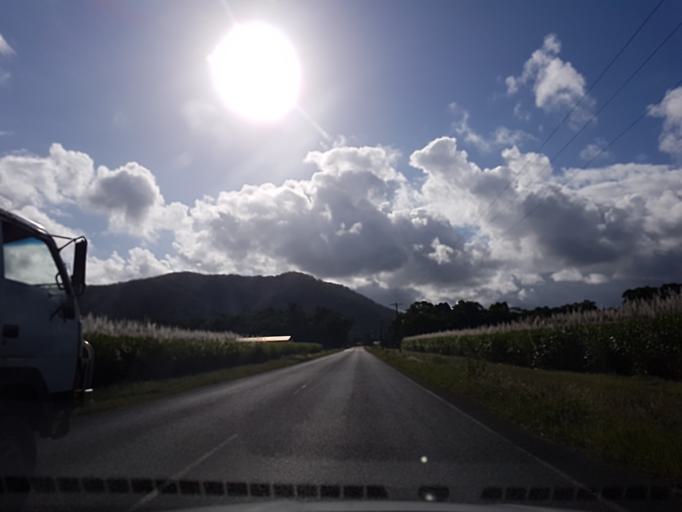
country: AU
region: Queensland
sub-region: Cairns
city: Port Douglas
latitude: -16.3080
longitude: 145.3930
